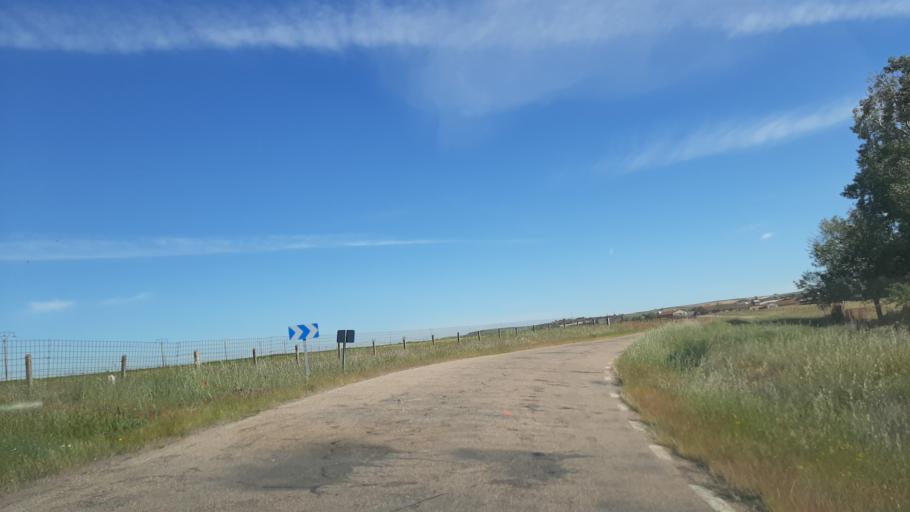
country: ES
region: Castille and Leon
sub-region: Provincia de Salamanca
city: Gajates
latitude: 40.7934
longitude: -5.3729
